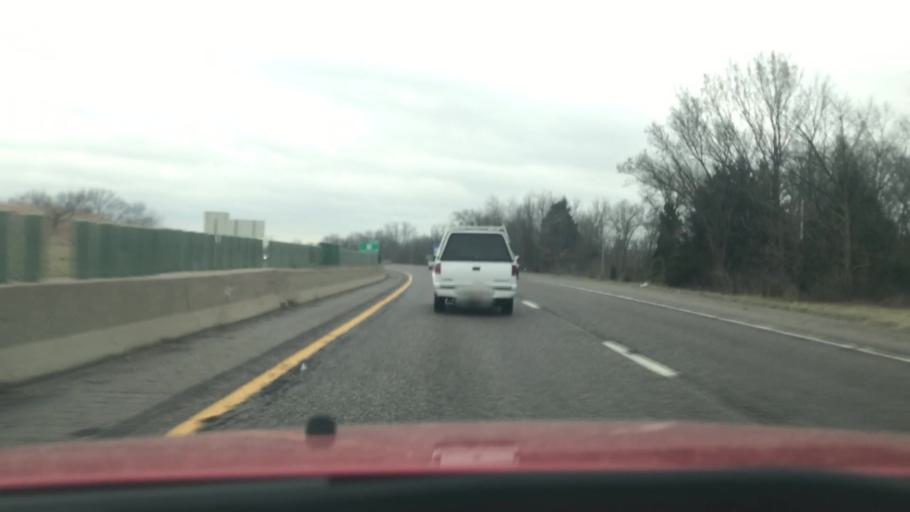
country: US
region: Missouri
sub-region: Saint Charles County
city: Wentzville
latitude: 38.8080
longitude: -90.8633
